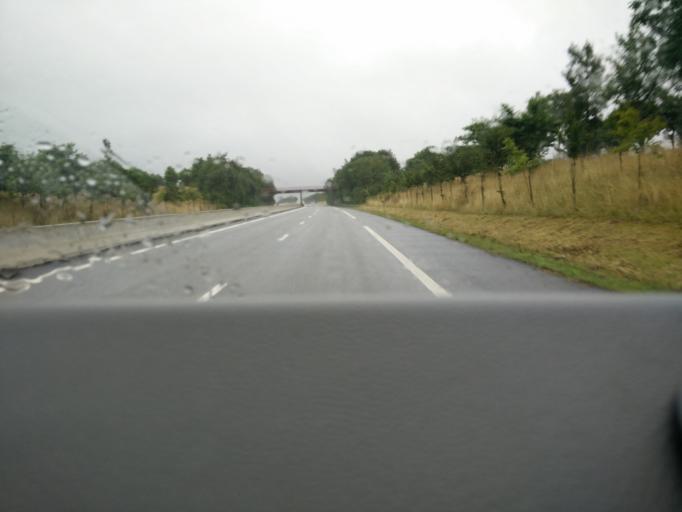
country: FR
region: Nord-Pas-de-Calais
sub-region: Departement du Pas-de-Calais
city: Saint-Pol-sur-Ternoise
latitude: 50.3674
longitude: 2.3281
